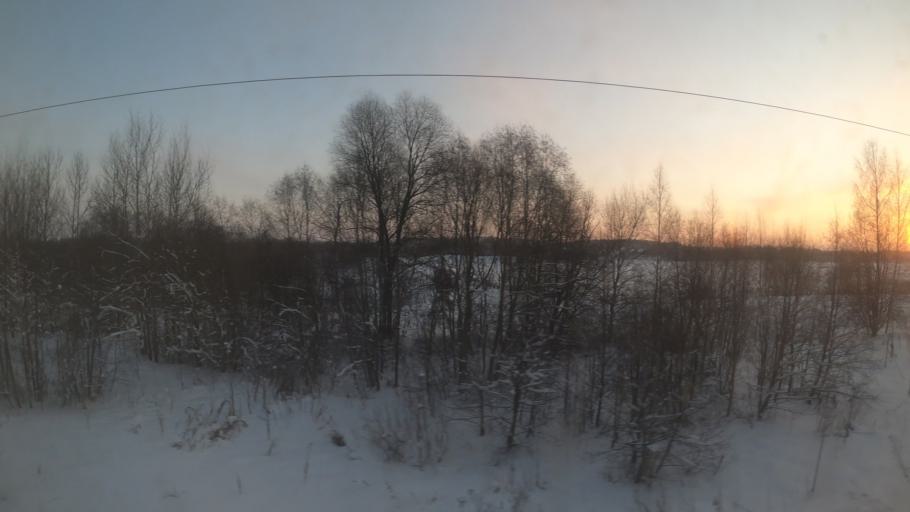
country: RU
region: Moskovskaya
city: Yermolino
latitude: 56.1529
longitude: 37.5029
